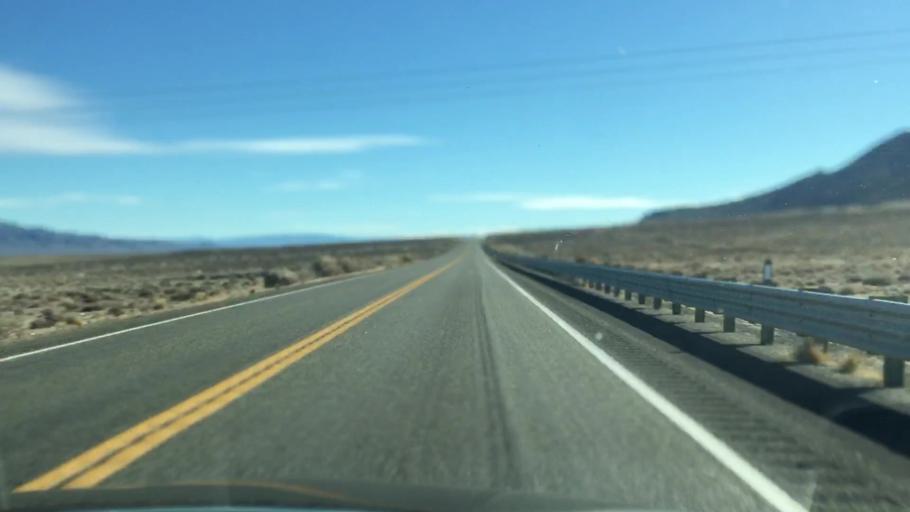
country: US
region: Nevada
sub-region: Mineral County
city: Hawthorne
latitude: 38.8119
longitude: -118.7652
